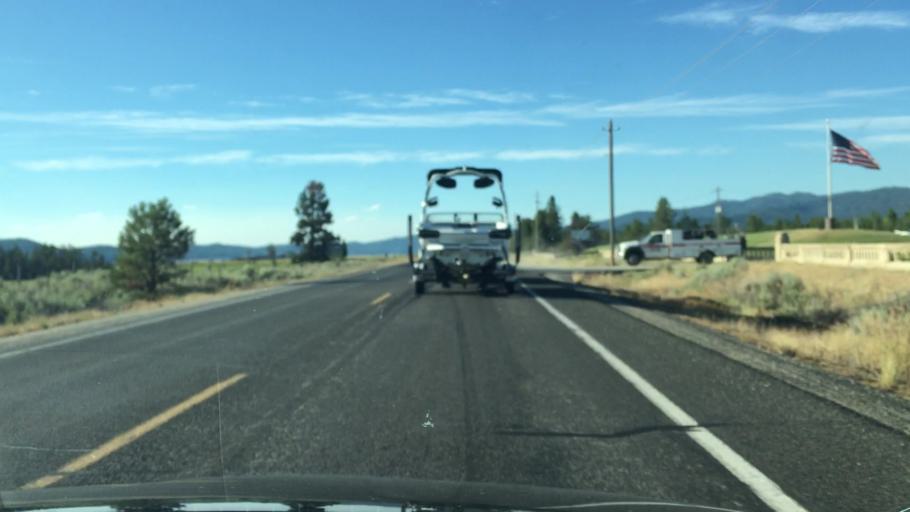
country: US
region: Idaho
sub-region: Valley County
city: Cascade
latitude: 44.4745
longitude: -115.9992
